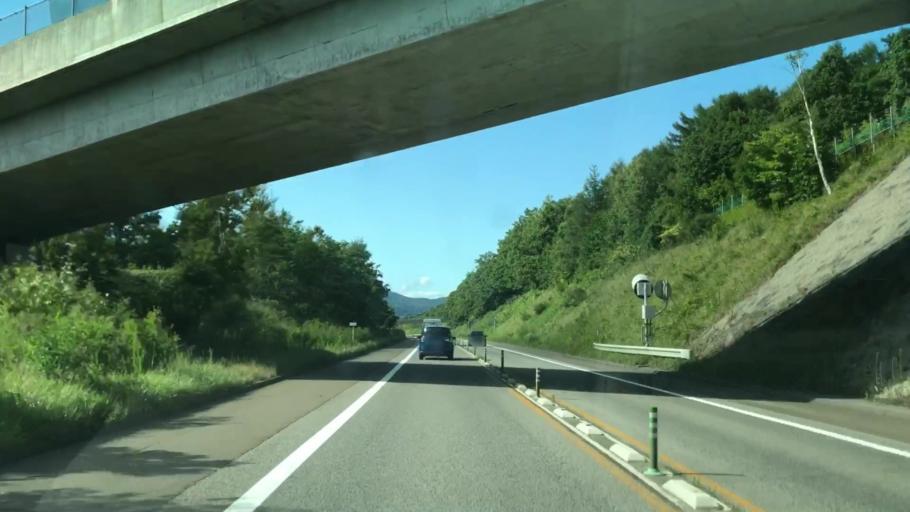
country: JP
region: Hokkaido
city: Date
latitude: 42.4731
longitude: 140.9044
